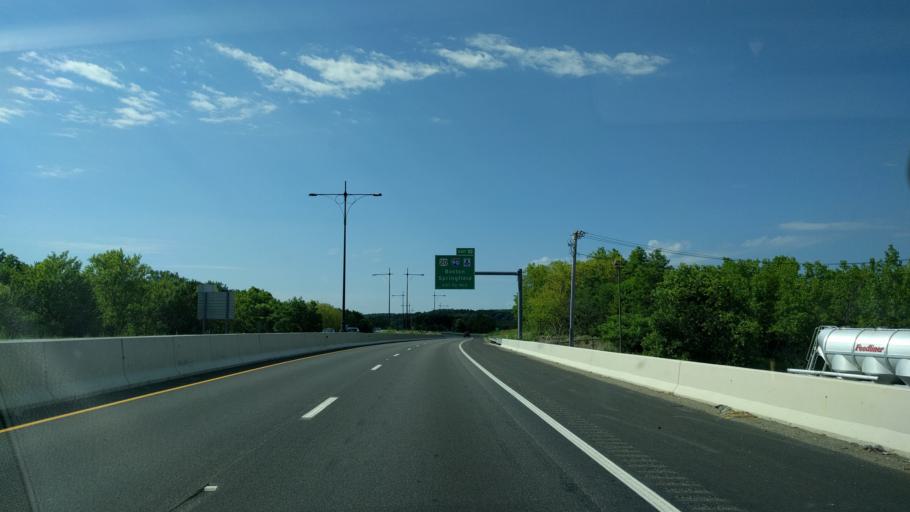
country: US
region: Massachusetts
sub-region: Worcester County
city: Sunderland
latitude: 42.2208
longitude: -71.7866
